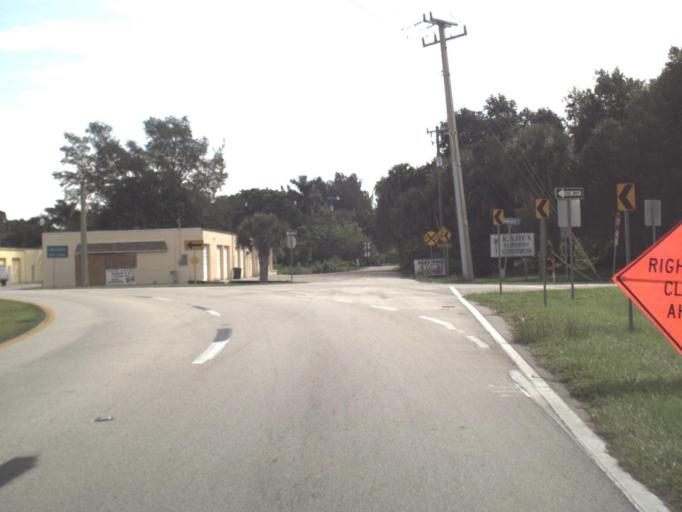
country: US
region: Florida
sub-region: Lee County
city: Fort Myers
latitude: 26.6472
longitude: -81.8563
